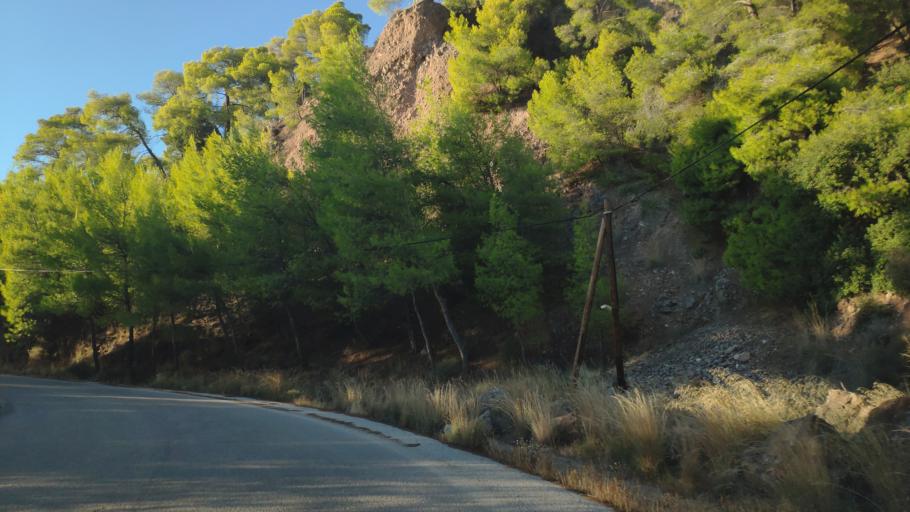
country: GR
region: Attica
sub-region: Nomos Piraios
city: Megalochori
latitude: 37.6073
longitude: 23.3305
